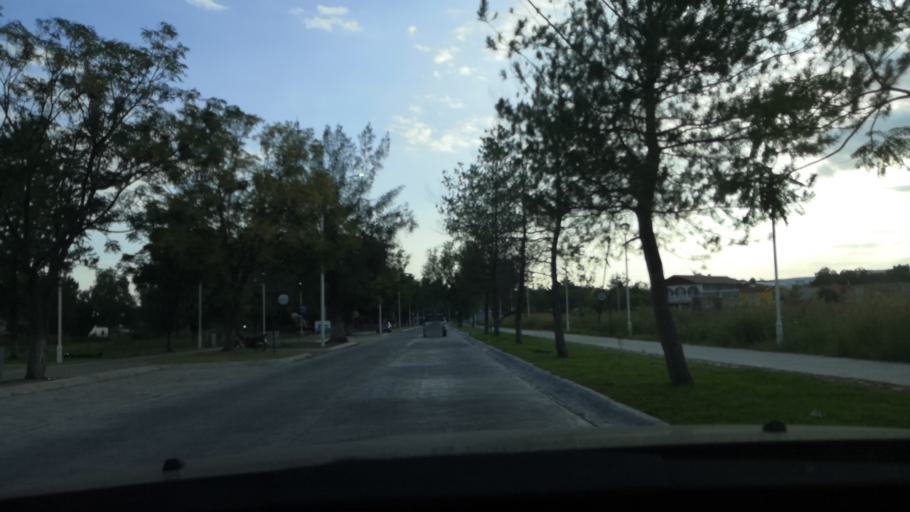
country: MX
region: Guanajuato
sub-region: San Francisco del Rincon
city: Estacion de San Francisco
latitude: 21.0286
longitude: -101.8325
